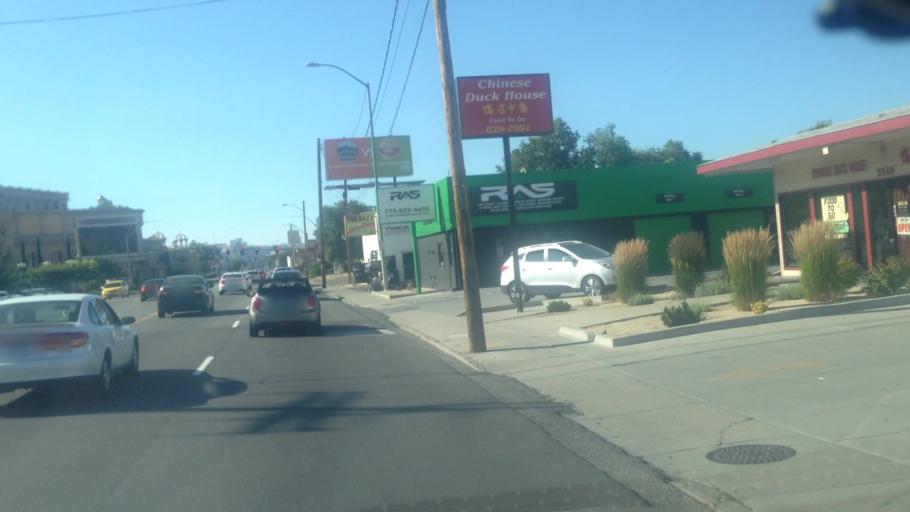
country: US
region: Nevada
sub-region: Washoe County
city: Reno
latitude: 39.4959
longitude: -119.7983
